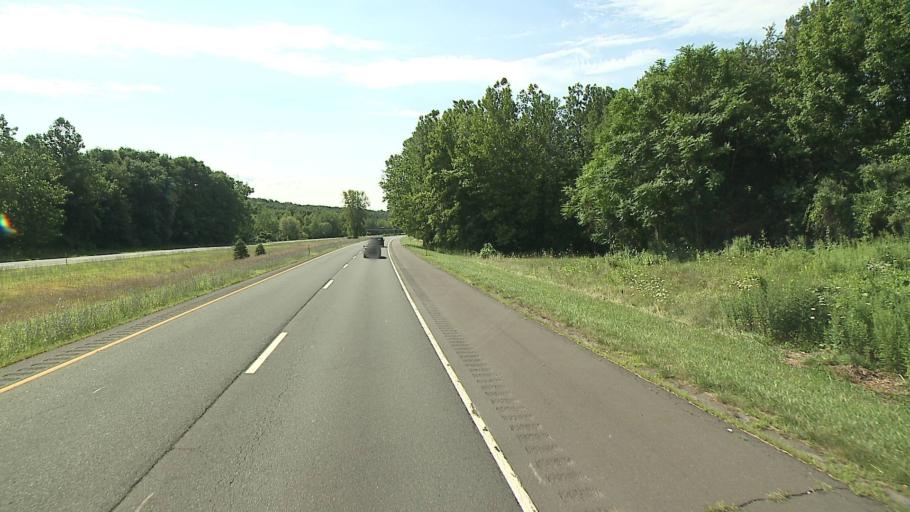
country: US
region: Connecticut
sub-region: Fairfield County
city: Danbury
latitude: 41.4600
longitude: -73.3981
